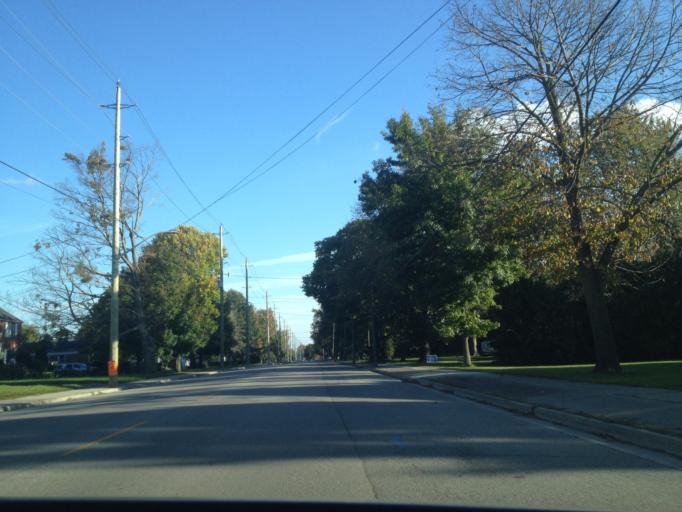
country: CA
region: Ontario
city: Delaware
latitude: 42.5998
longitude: -81.6017
